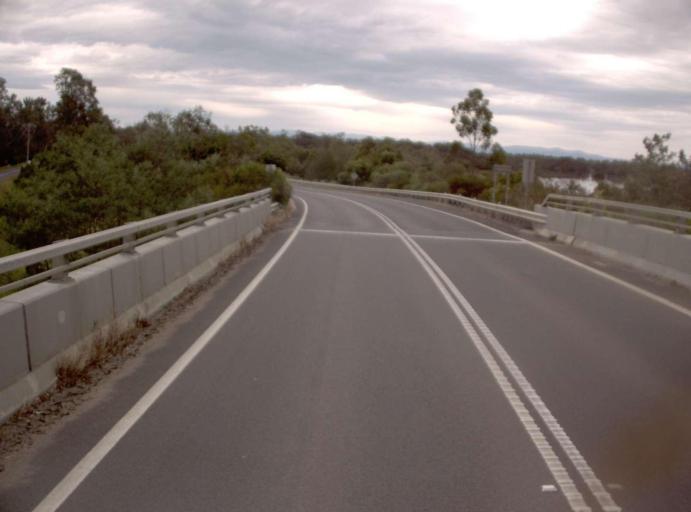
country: AU
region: Victoria
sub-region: Wellington
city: Sale
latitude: -38.1425
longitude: 147.0814
